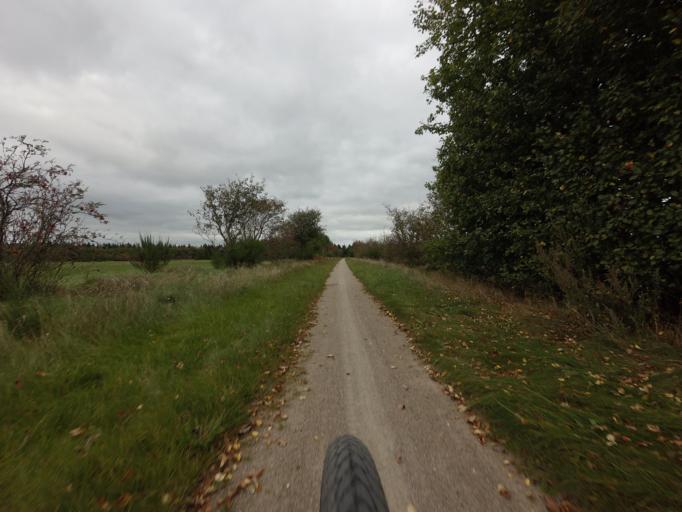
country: DK
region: South Denmark
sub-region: Billund Kommune
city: Grindsted
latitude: 55.7922
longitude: 8.9748
